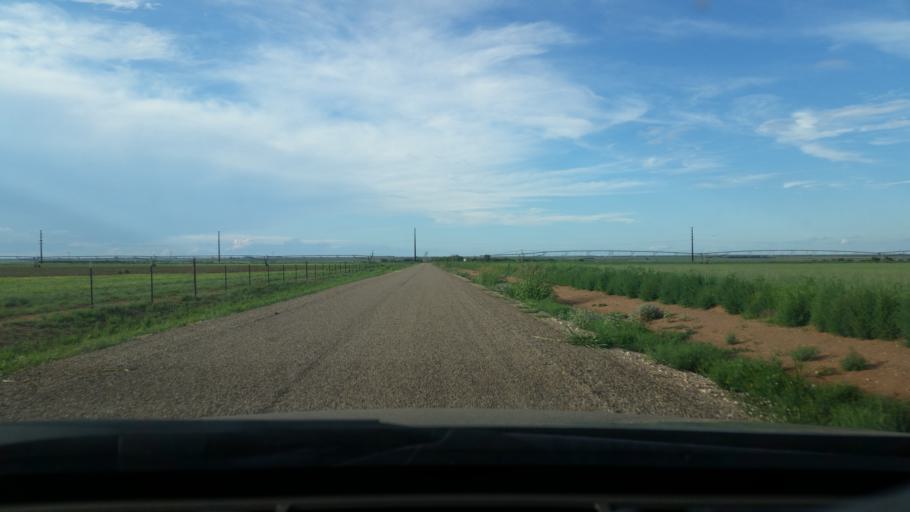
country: US
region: New Mexico
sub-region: Curry County
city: Clovis
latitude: 34.5008
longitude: -103.1788
